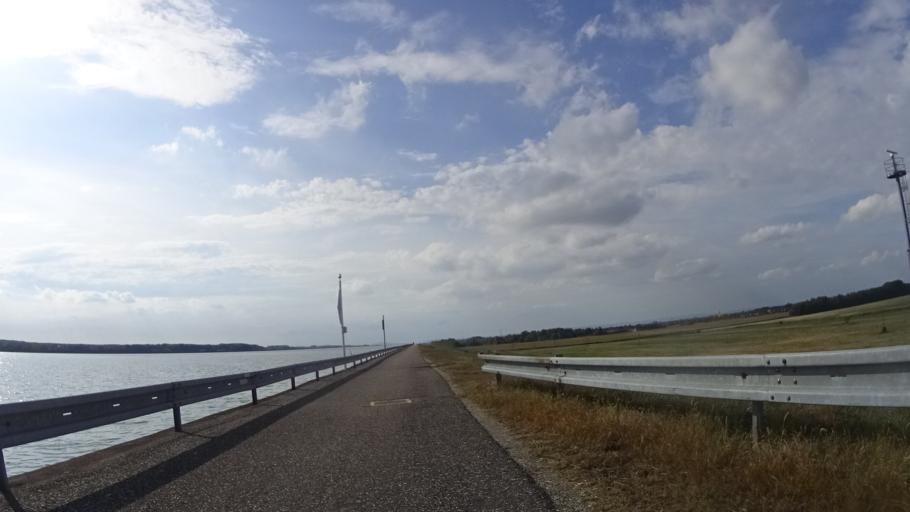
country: HU
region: Gyor-Moson-Sopron
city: Asvanyraro
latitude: 47.9305
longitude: 17.4703
